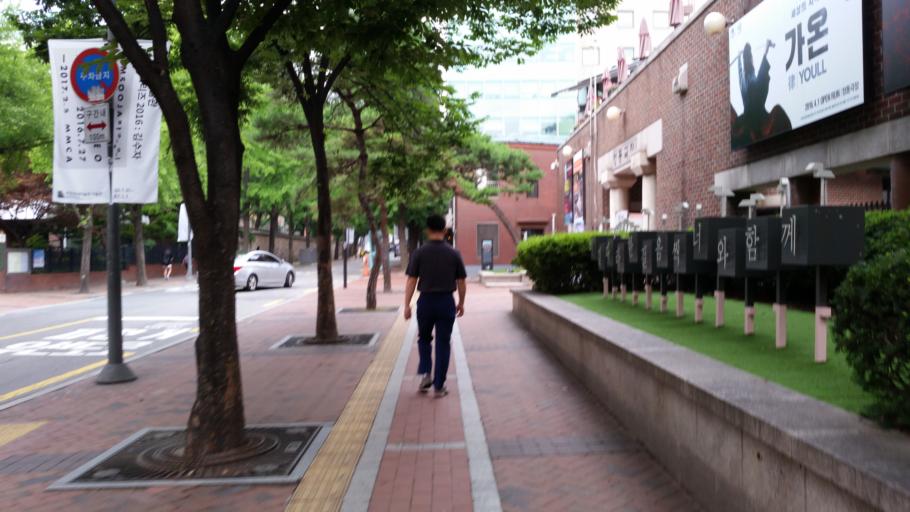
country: KR
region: Seoul
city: Seoul
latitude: 37.5656
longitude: 126.9730
